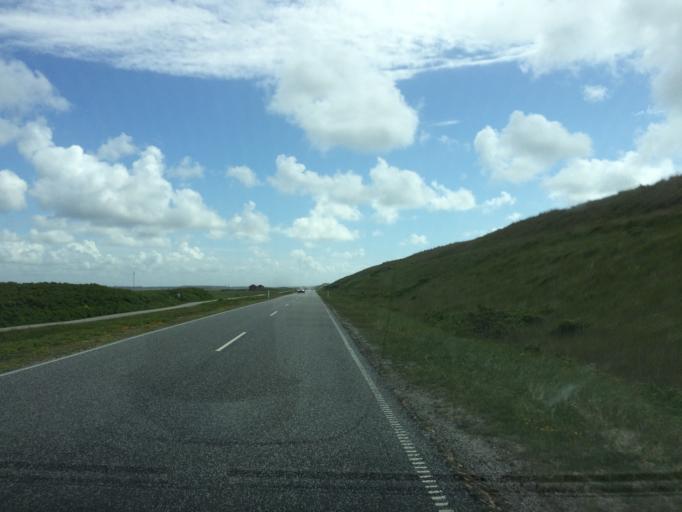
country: DK
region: Central Jutland
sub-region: Holstebro Kommune
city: Ulfborg
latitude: 56.3557
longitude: 8.1223
